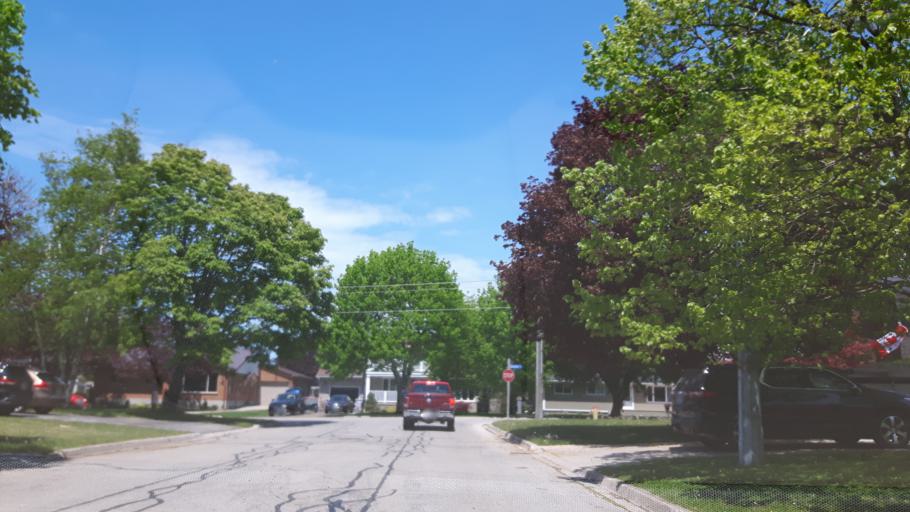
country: CA
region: Ontario
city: Goderich
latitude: 43.7312
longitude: -81.7200
